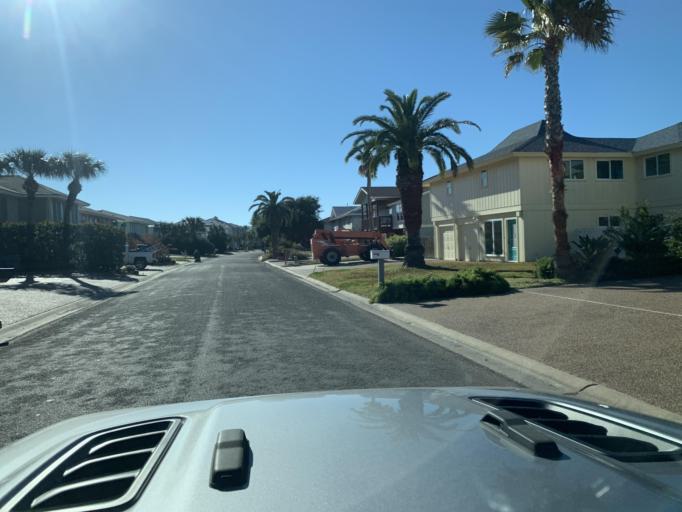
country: US
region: Texas
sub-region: Aransas County
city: Fulton
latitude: 28.0355
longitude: -97.0296
